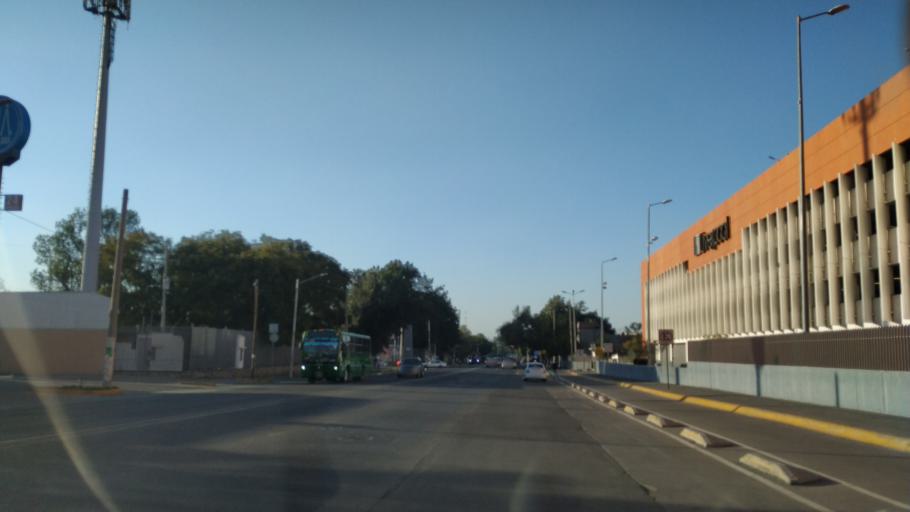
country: MX
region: Jalisco
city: Tlaquepaque
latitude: 20.6485
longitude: -103.3221
